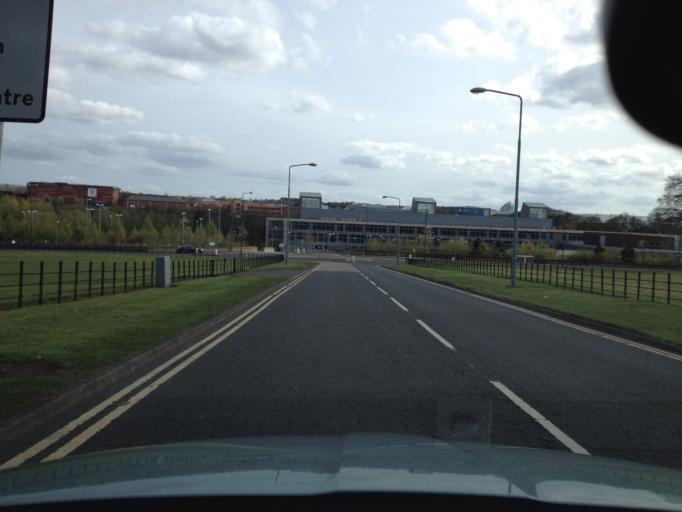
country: GB
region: Scotland
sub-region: West Lothian
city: Livingston
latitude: 55.8893
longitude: -3.5143
